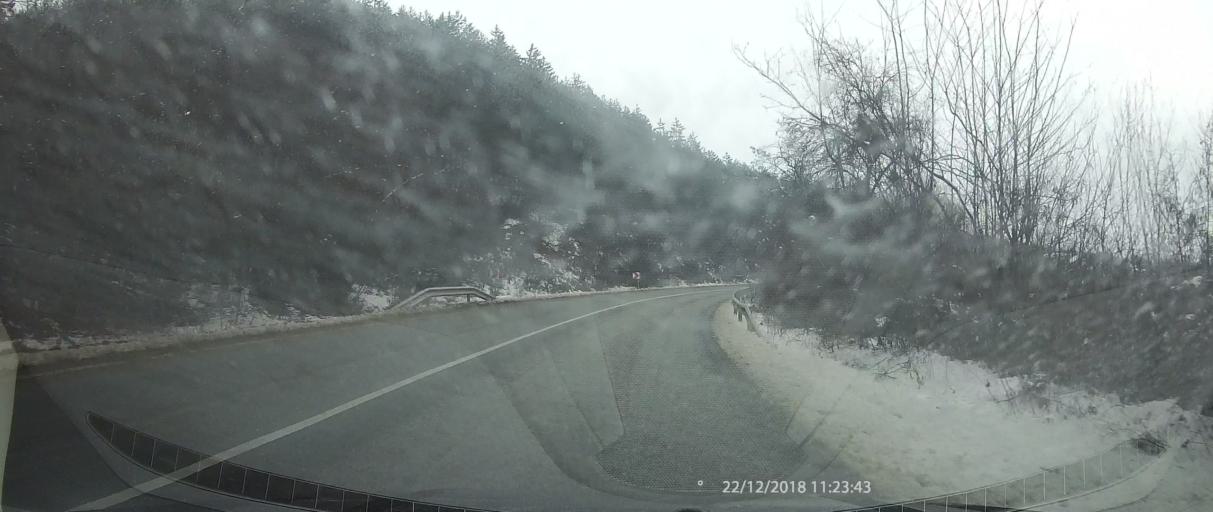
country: BG
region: Kyustendil
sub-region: Obshtina Boboshevo
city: Boboshevo
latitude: 42.2569
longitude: 22.8836
